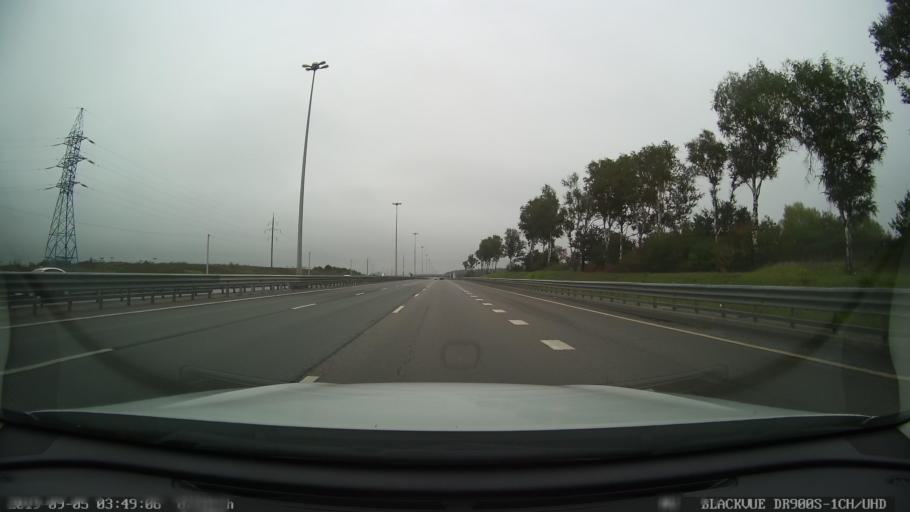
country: RU
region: Moscow
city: Khimki
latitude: 55.9314
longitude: 37.4005
